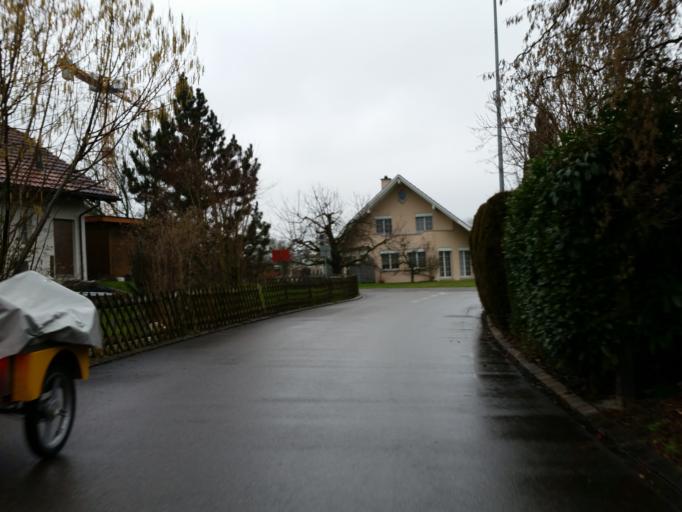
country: CH
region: Thurgau
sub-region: Arbon District
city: Egnach
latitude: 47.5472
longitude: 9.3746
